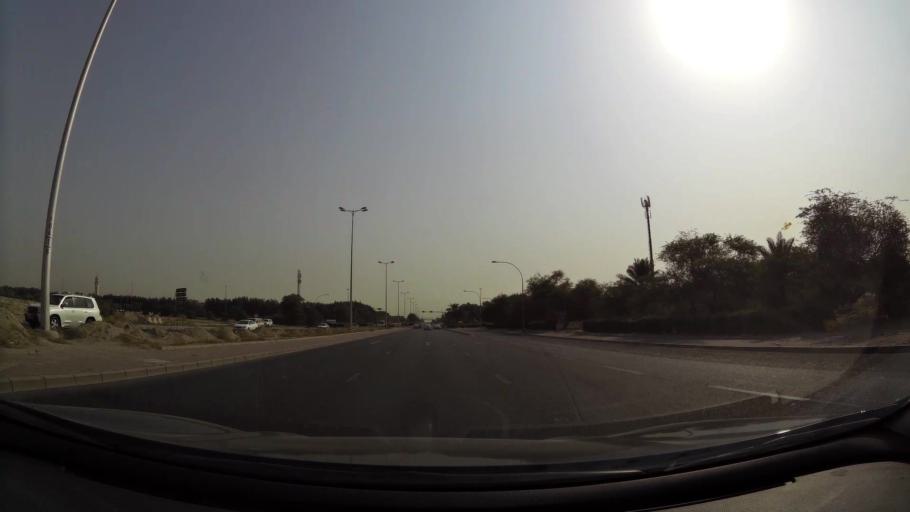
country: KW
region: Al Asimah
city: Ar Rabiyah
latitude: 29.2746
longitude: 47.8625
